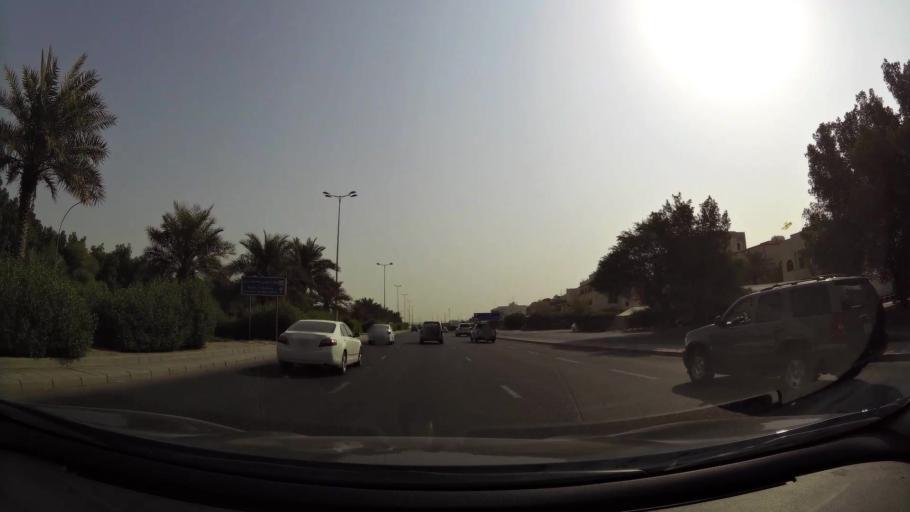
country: KW
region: Al Asimah
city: Ar Rabiyah
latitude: 29.2746
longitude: 47.8654
